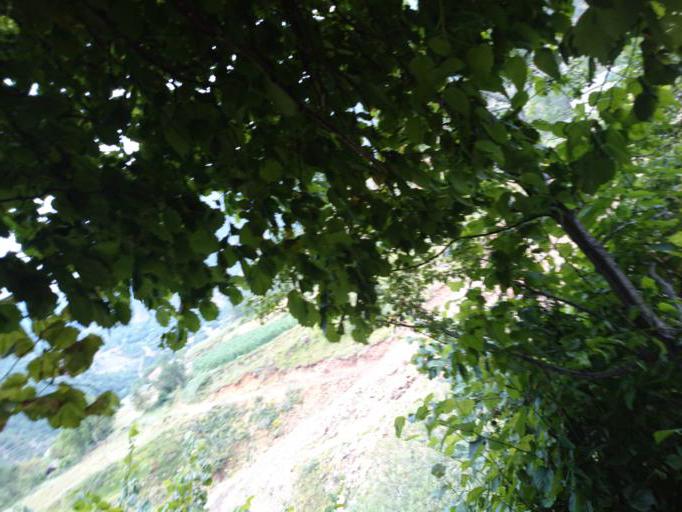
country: AL
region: Diber
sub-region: Rrethi i Dibres
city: Fushe-Lure
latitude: 41.7602
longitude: 20.2246
